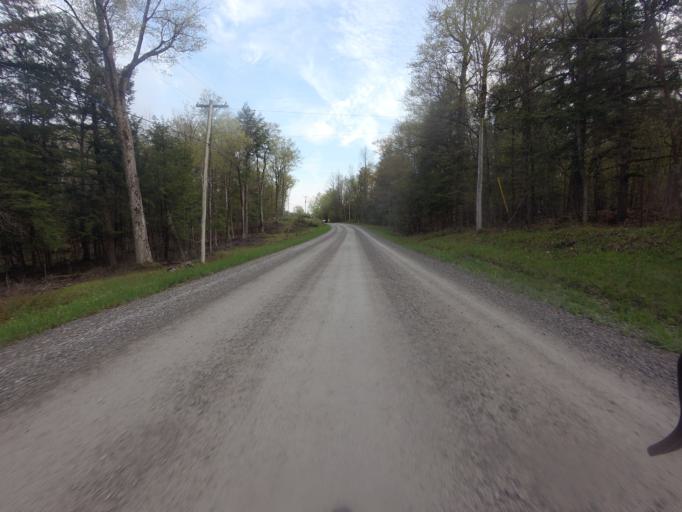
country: CA
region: Ontario
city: Carleton Place
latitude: 45.1962
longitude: -76.3270
